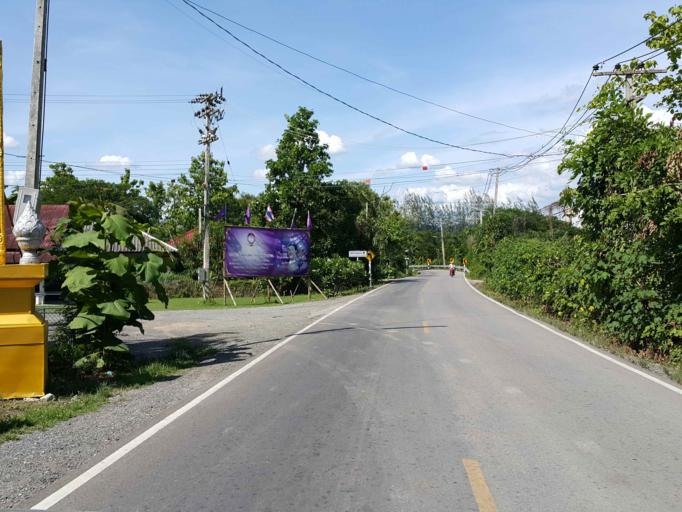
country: TH
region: Chiang Mai
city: San Kamphaeng
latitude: 18.7723
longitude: 99.1544
